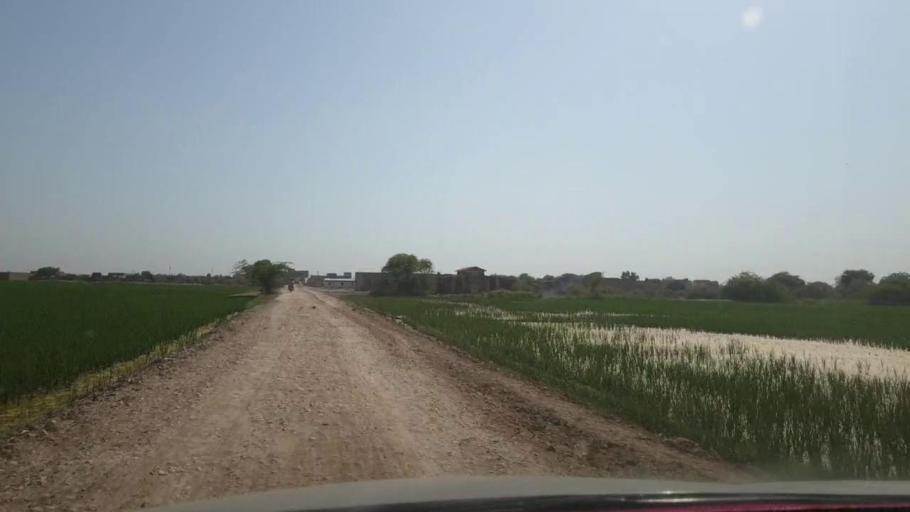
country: PK
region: Sindh
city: Nasirabad
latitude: 27.3492
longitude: 67.8425
